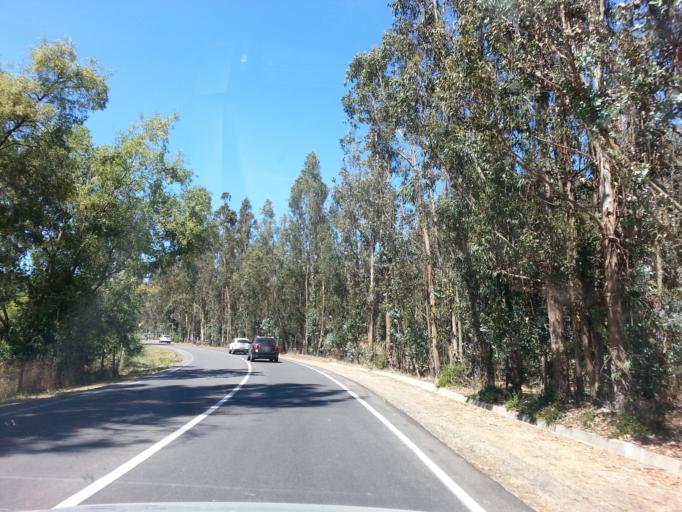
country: CL
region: Valparaiso
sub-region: Provincia de Marga Marga
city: Villa Alemana
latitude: -33.1864
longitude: -71.3681
